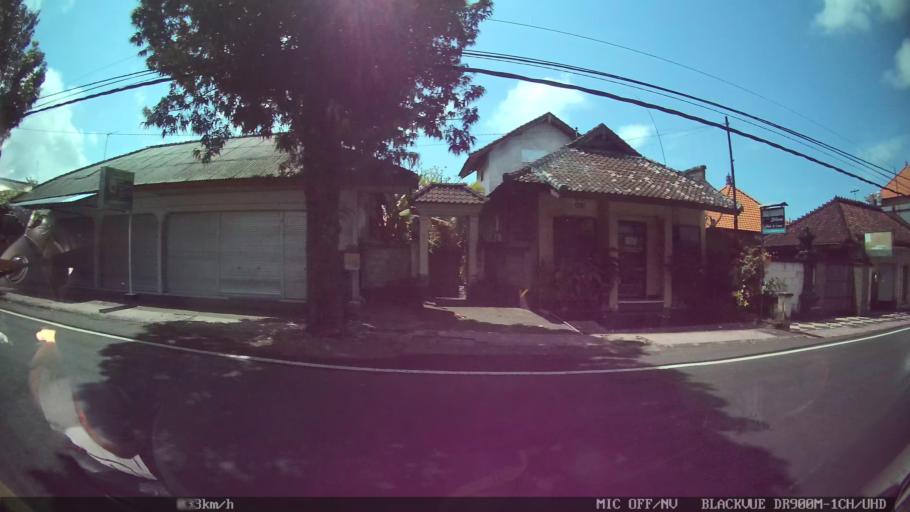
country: ID
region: Bali
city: Banjar Pasekan
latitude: -8.6027
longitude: 115.2740
